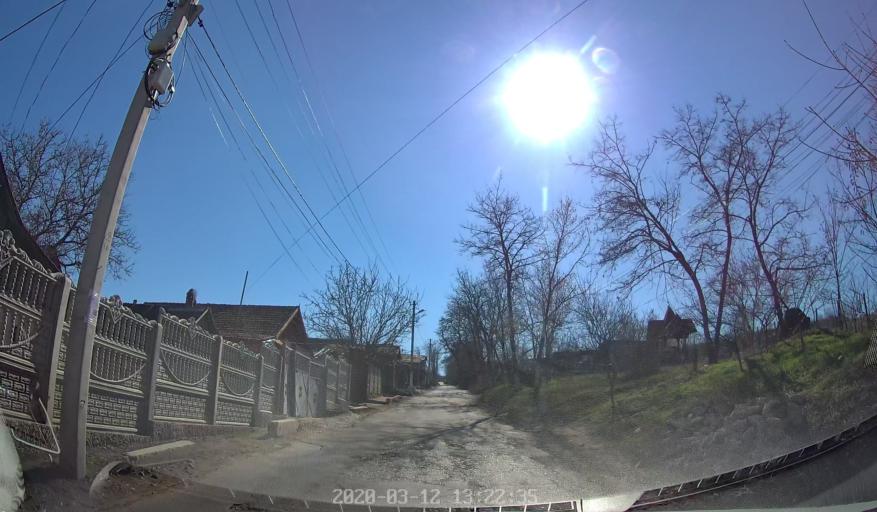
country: MD
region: Laloveni
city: Ialoveni
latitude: 46.9463
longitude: 28.8364
